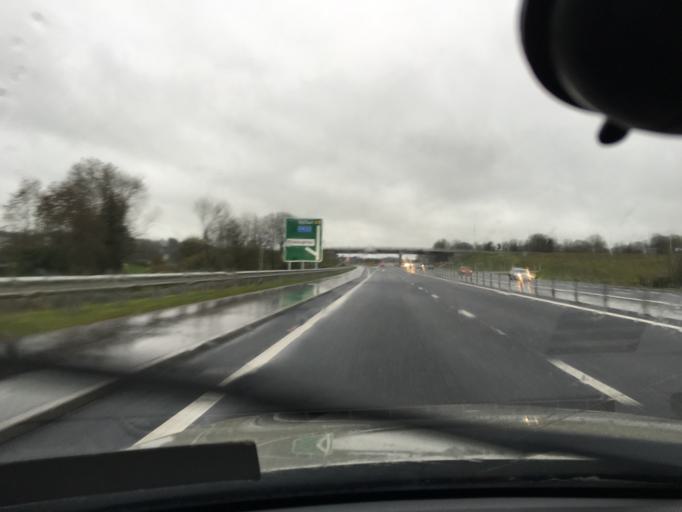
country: GB
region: Northern Ireland
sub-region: Larne District
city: Larne
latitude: 54.8193
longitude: -5.8942
